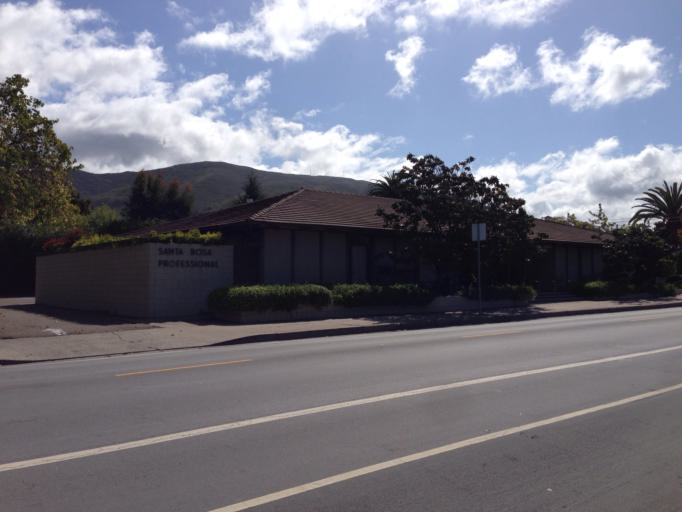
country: US
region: California
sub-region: San Luis Obispo County
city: San Luis Obispo
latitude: 35.2801
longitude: -120.6578
